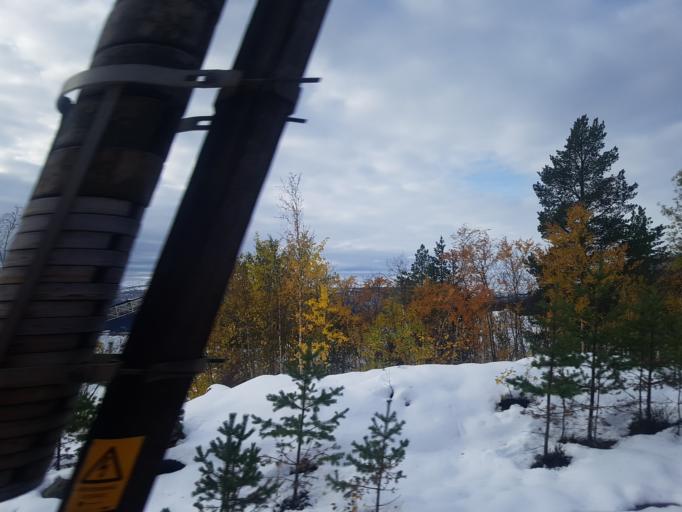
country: NO
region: Oppland
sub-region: Dovre
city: Dombas
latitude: 62.0954
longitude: 9.0446
